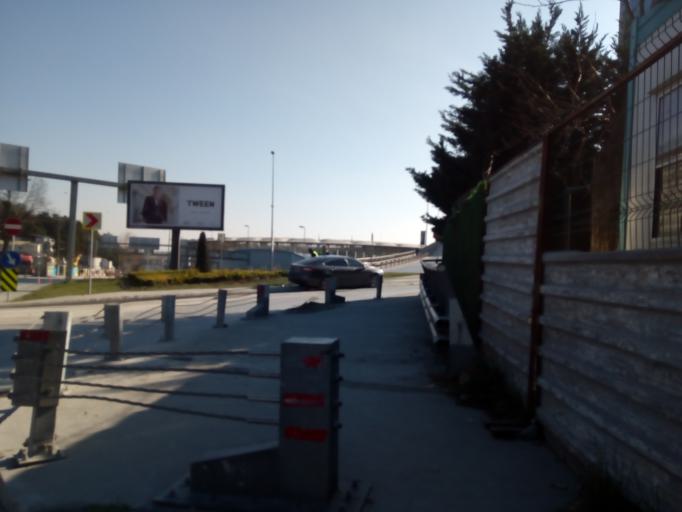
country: TR
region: Istanbul
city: Sisli
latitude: 41.0424
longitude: 28.9931
